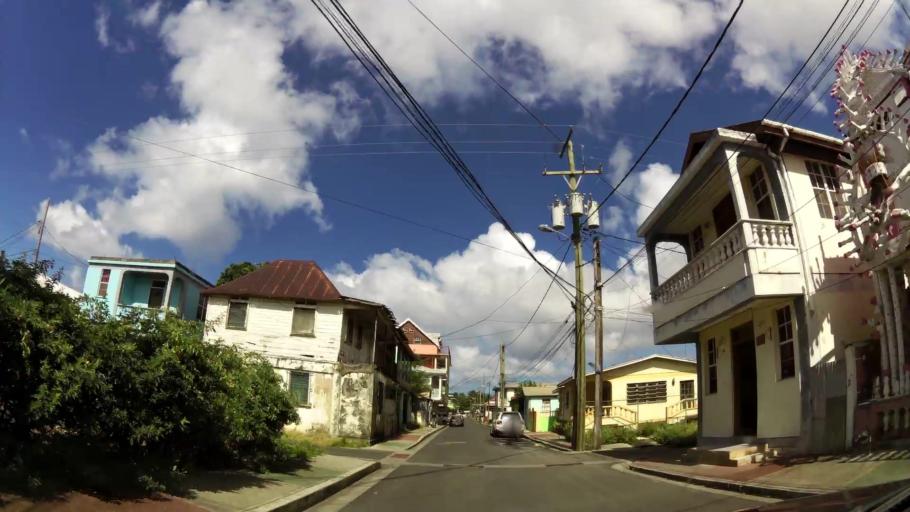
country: DM
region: Saint John
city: Portsmouth
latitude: 15.5756
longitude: -61.4562
